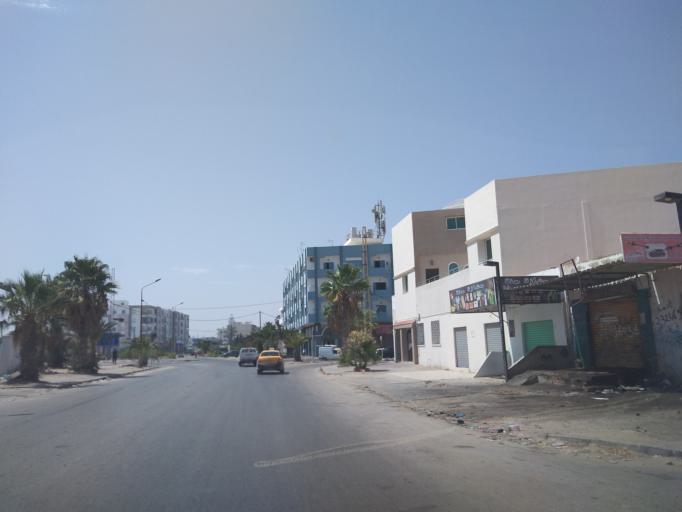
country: TN
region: Safaqis
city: Sfax
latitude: 34.7410
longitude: 10.7398
